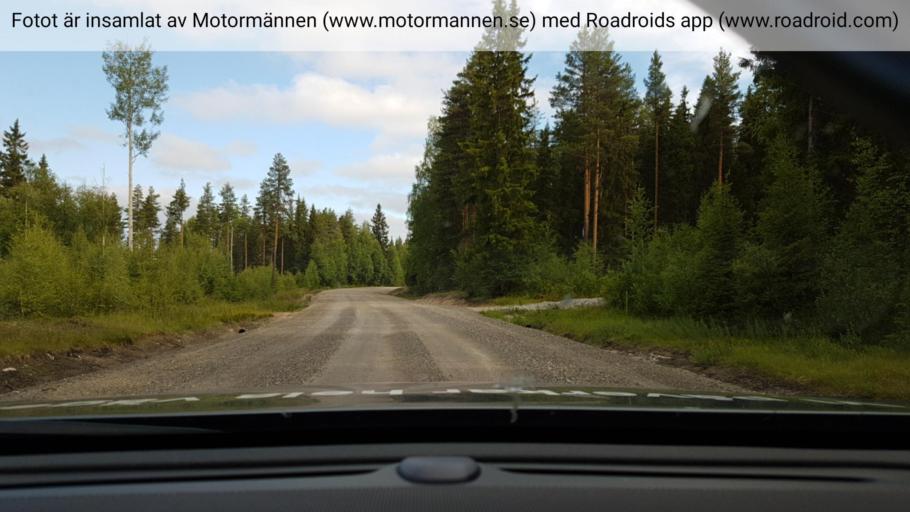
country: SE
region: Vaesterbotten
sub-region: Norsjo Kommun
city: Norsjoe
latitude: 64.6392
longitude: 19.2858
